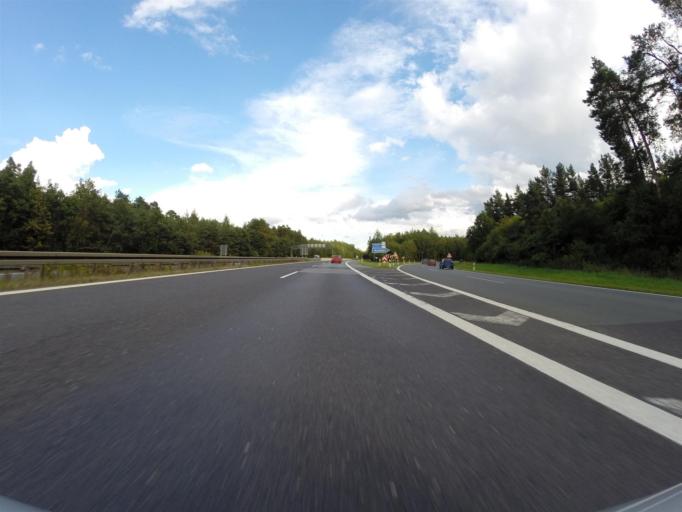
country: DE
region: Bavaria
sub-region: Regierungsbezirk Mittelfranken
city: Feucht
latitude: 49.3665
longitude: 11.1906
